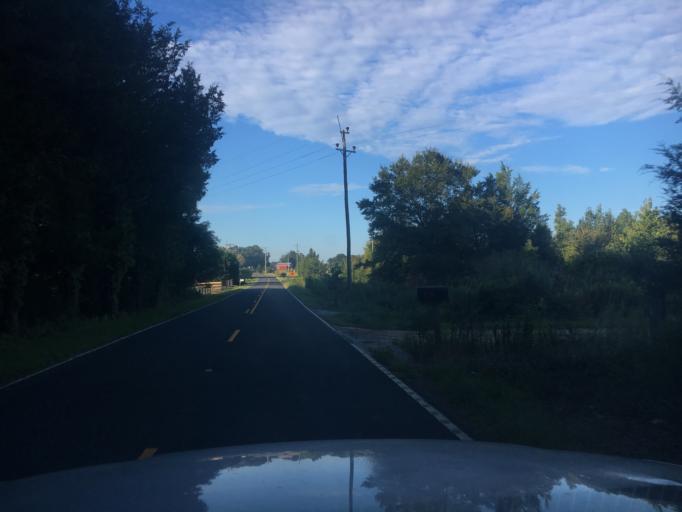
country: US
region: South Carolina
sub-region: Spartanburg County
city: Woodruff
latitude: 34.6343
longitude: -82.0288
